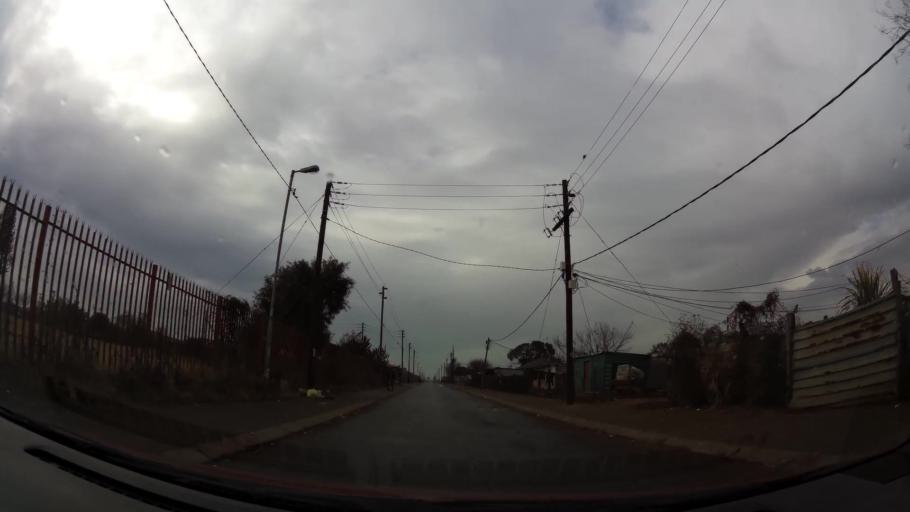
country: ZA
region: Gauteng
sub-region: City of Johannesburg Metropolitan Municipality
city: Soweto
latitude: -26.2823
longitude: 27.8431
